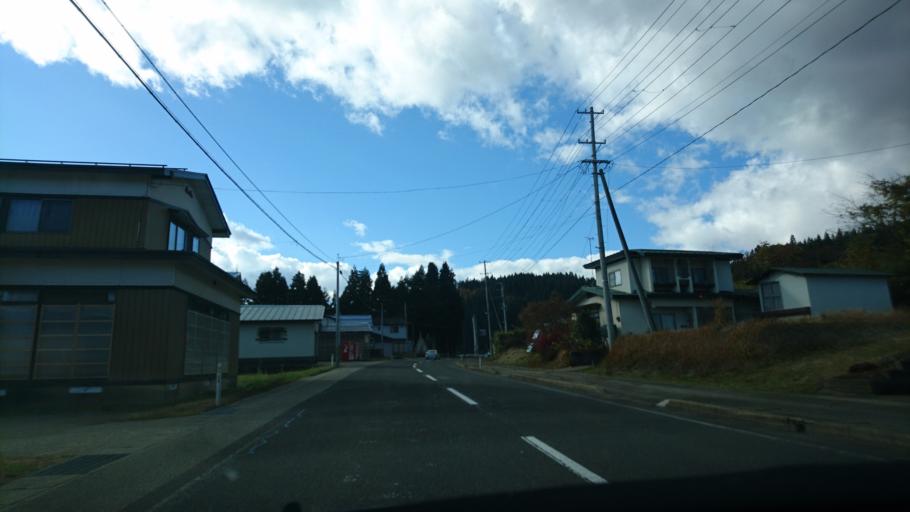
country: JP
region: Akita
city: Yuzawa
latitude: 39.2718
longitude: 140.3685
